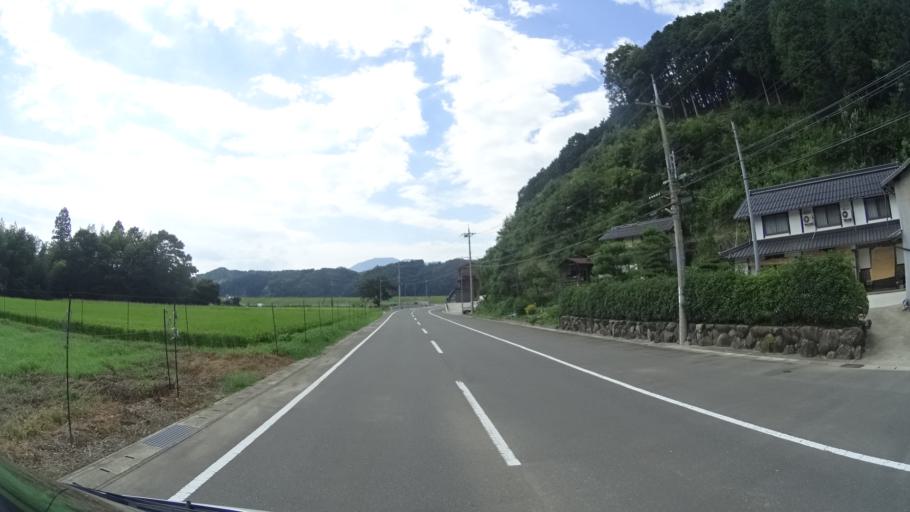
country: JP
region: Kyoto
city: Fukuchiyama
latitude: 35.3766
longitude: 135.1441
